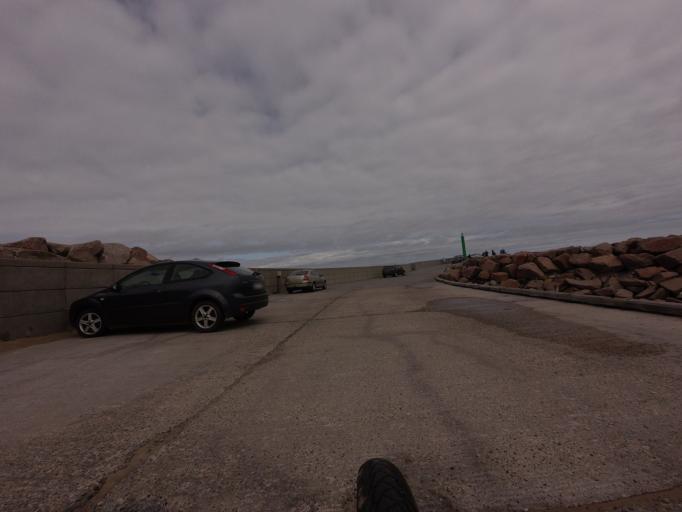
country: DK
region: North Denmark
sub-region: Hjorring Kommune
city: Hirtshals
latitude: 57.5959
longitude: 9.9581
